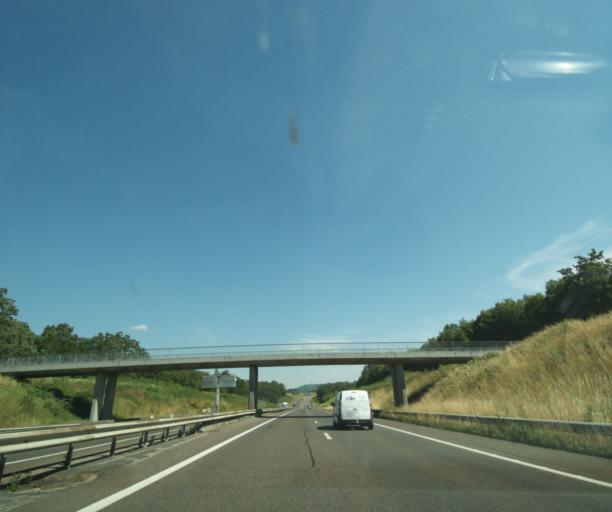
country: FR
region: Lorraine
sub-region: Departement de Meurthe-et-Moselle
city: Dommartin-les-Toul
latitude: 48.6416
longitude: 5.8804
